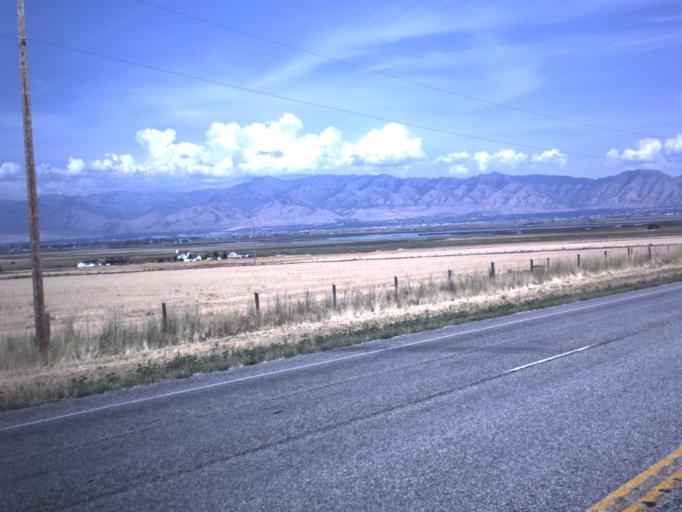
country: US
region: Utah
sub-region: Cache County
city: Mendon
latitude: 41.7536
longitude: -111.9916
